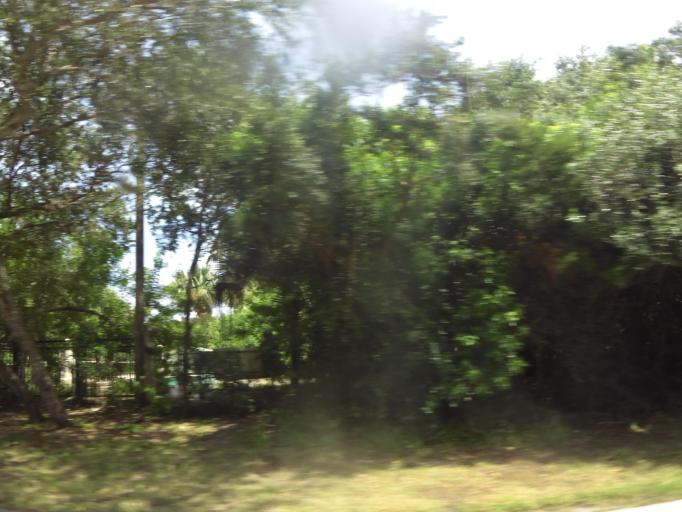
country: US
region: Florida
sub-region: Volusia County
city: Ponce Inlet
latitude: 29.0876
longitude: -80.9341
